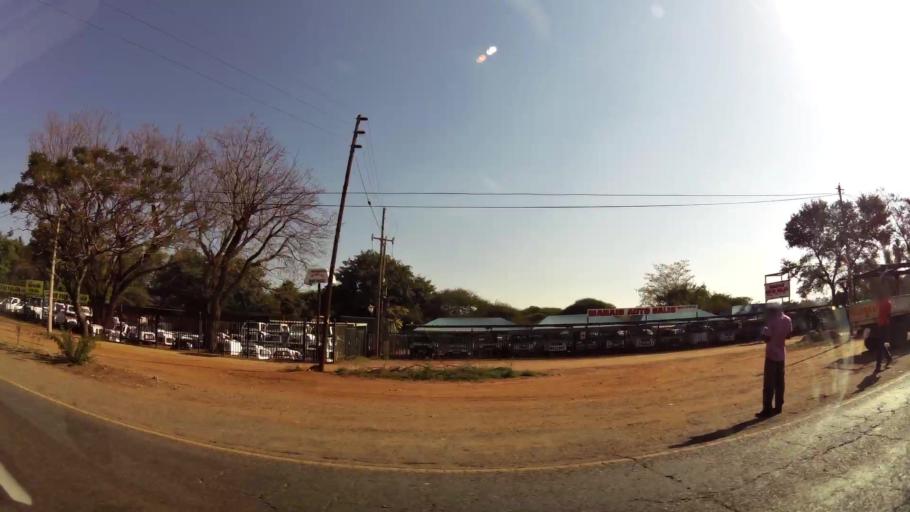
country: ZA
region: Gauteng
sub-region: City of Tshwane Metropolitan Municipality
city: Pretoria
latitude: -25.6702
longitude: 28.1936
